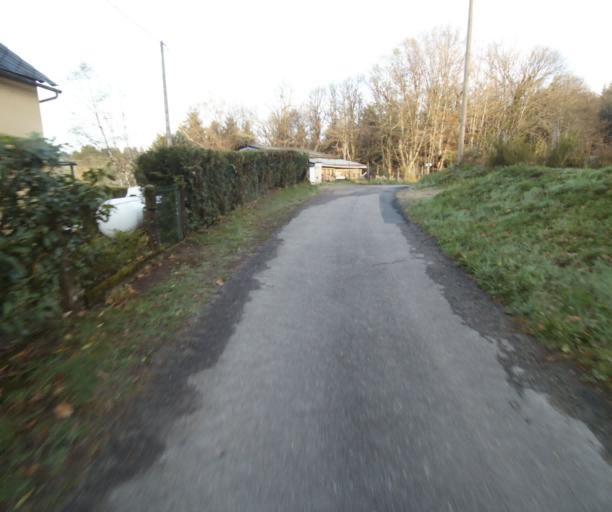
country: FR
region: Limousin
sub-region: Departement de la Correze
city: Correze
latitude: 45.3088
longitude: 1.8489
